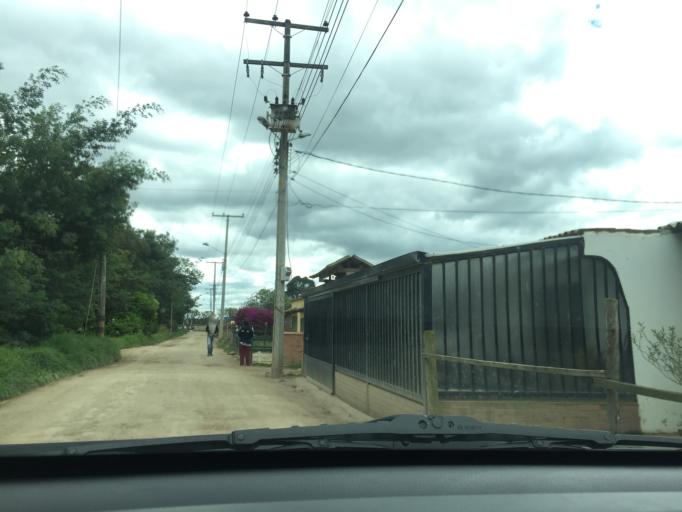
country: CO
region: Cundinamarca
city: Zipaquira
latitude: 5.0040
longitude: -73.9762
